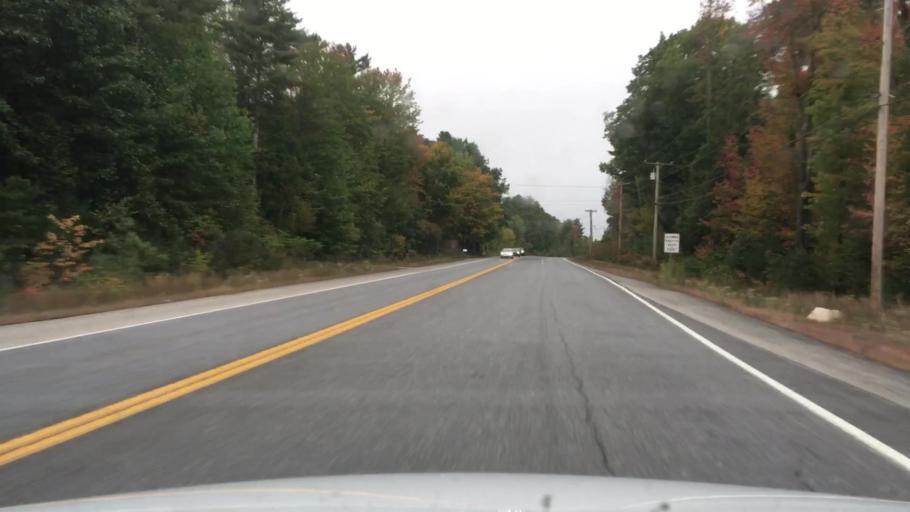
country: US
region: Maine
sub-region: Cumberland County
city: New Gloucester
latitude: 43.9730
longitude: -70.3644
